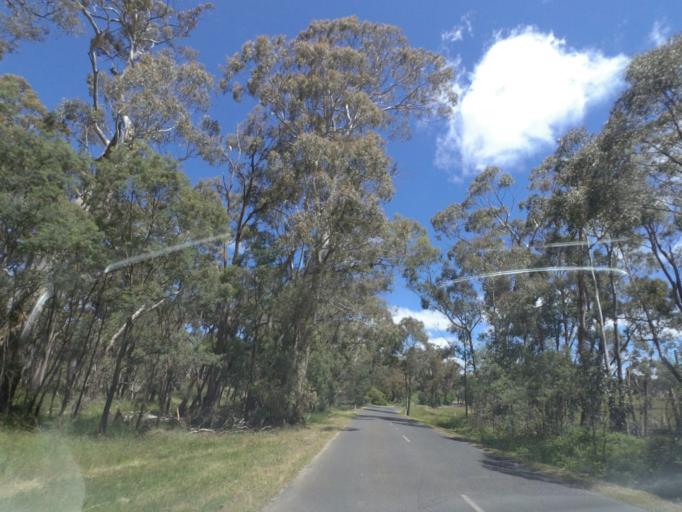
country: AU
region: Victoria
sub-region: Mount Alexander
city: Castlemaine
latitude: -37.3060
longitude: 144.1882
